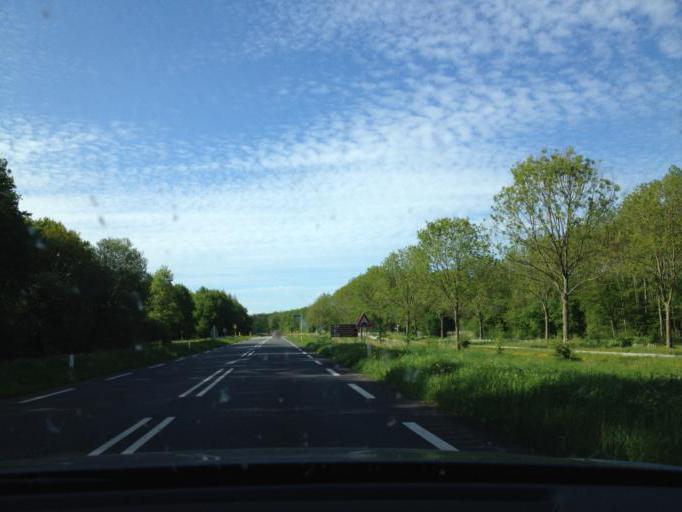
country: NL
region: Gelderland
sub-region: Gemeente Nijkerk
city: Nijkerk
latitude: 52.2701
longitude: 5.4519
